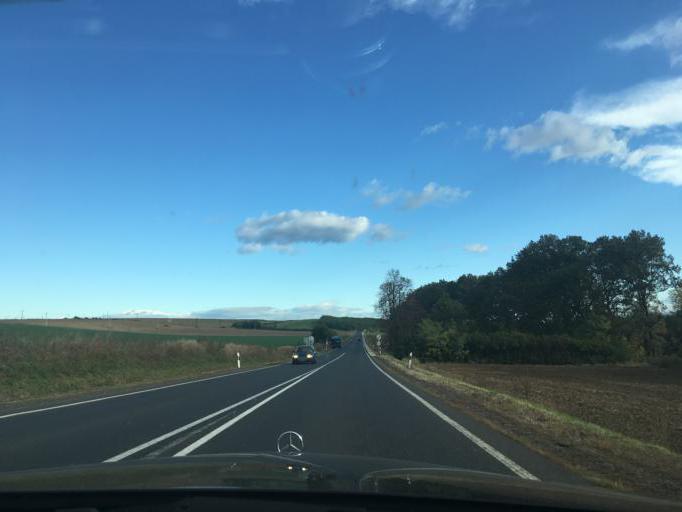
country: HU
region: Borsod-Abauj-Zemplen
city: Encs
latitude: 48.3650
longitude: 21.1401
